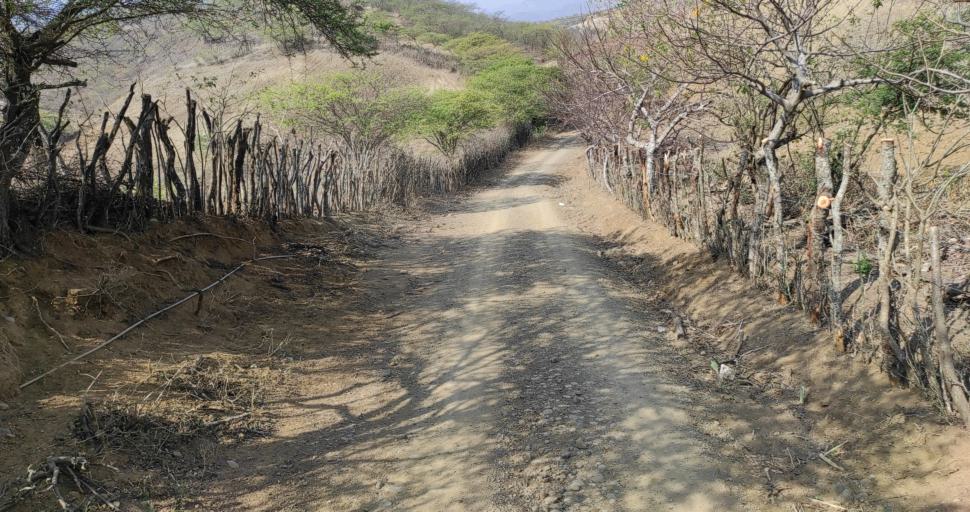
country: EC
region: Loja
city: Catacocha
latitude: -4.0095
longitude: -79.7007
